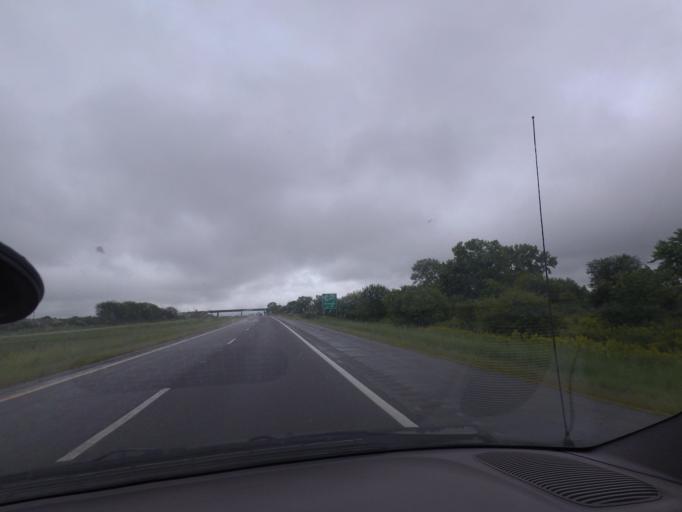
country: US
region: Illinois
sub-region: Champaign County
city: Champaign
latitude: 40.1201
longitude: -88.3183
